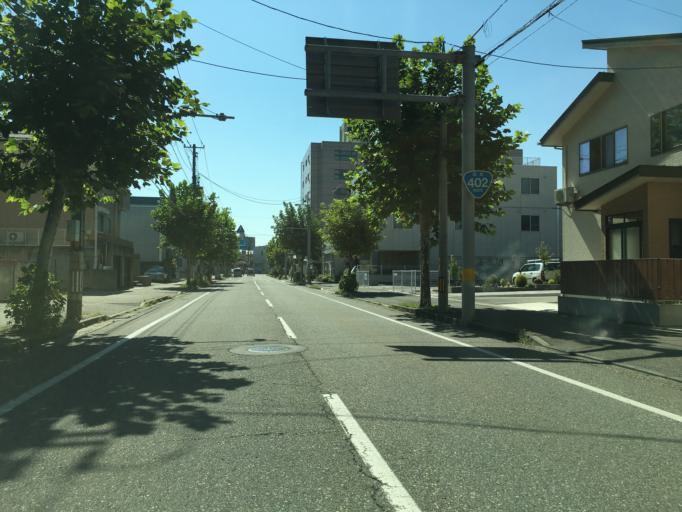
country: JP
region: Niigata
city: Niigata-shi
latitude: 37.9067
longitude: 139.0113
